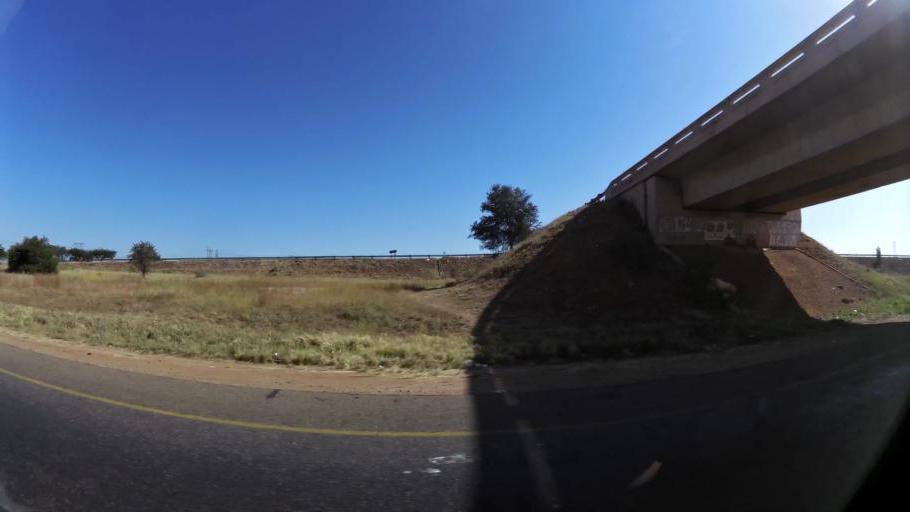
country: ZA
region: Gauteng
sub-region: City of Tshwane Metropolitan Municipality
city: Mabopane
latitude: -25.5568
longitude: 28.1081
